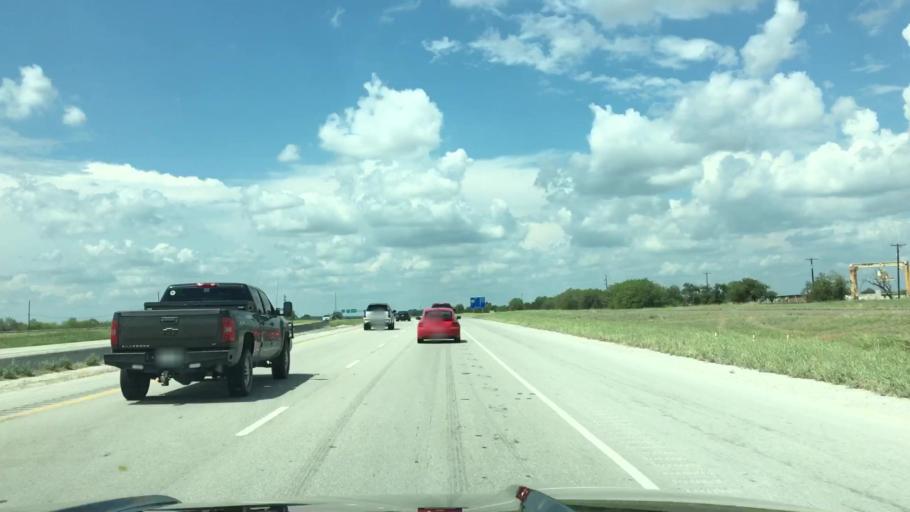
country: US
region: Texas
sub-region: Wise County
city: Rhome
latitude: 33.0362
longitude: -97.4528
